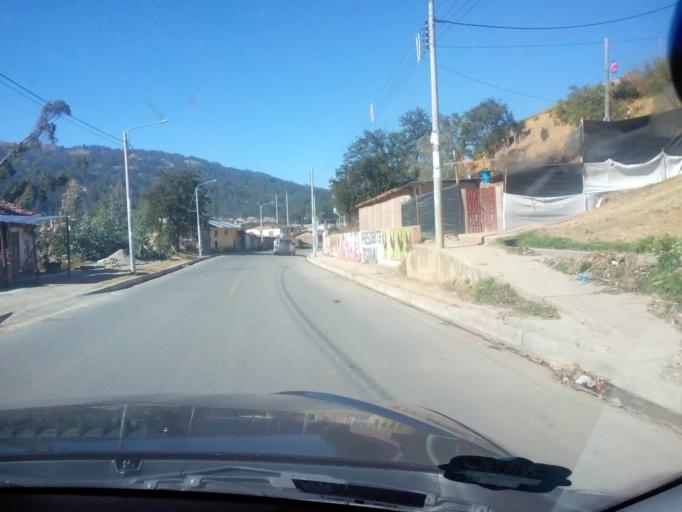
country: PE
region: Apurimac
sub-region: Provincia de Andahuaylas
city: Talavera
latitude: -13.6590
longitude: -73.4363
